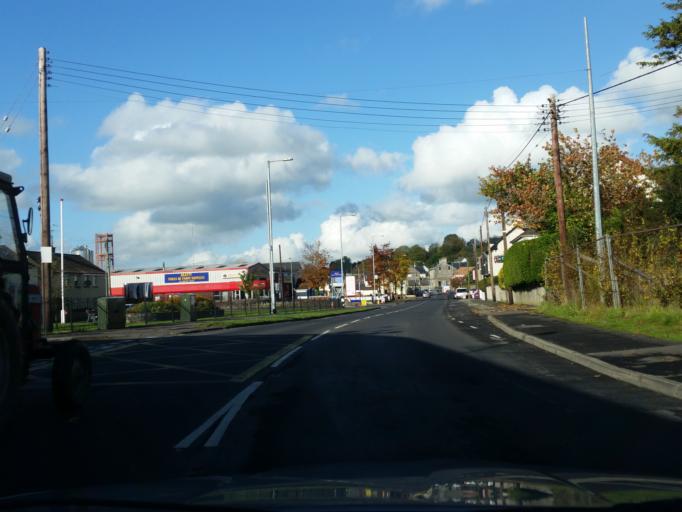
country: GB
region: Northern Ireland
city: Lisnaskea
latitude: 54.2486
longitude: -7.4412
